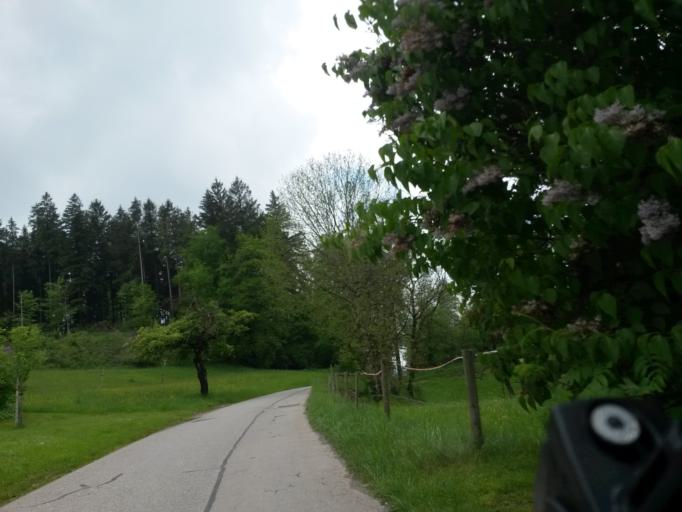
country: DE
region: Baden-Wuerttemberg
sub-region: Tuebingen Region
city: Wolfegg
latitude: 47.8653
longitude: 9.7940
